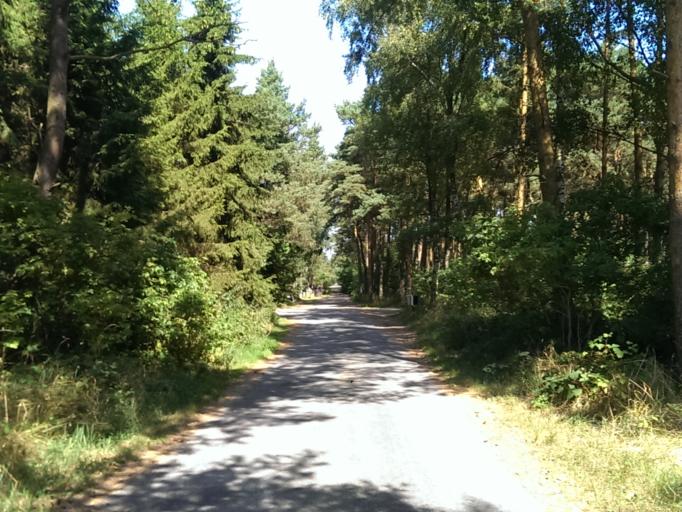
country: SE
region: Skane
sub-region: Simrishamns Kommun
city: Simrishamn
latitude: 55.4292
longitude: 14.2237
